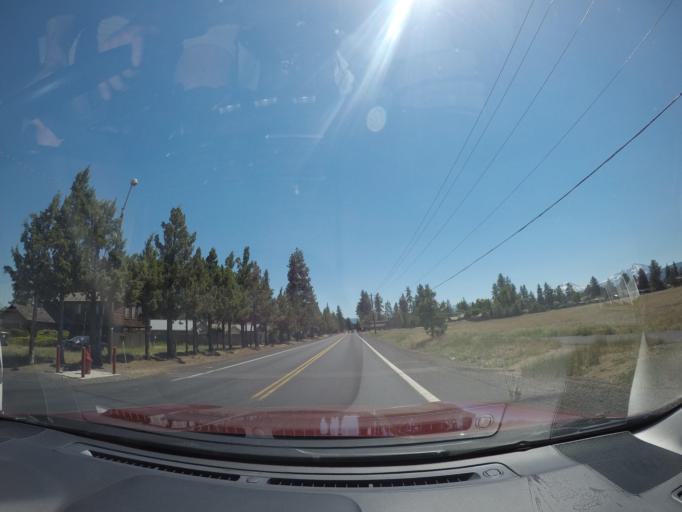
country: US
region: Oregon
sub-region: Deschutes County
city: Sisters
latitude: 44.2949
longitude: -121.5437
